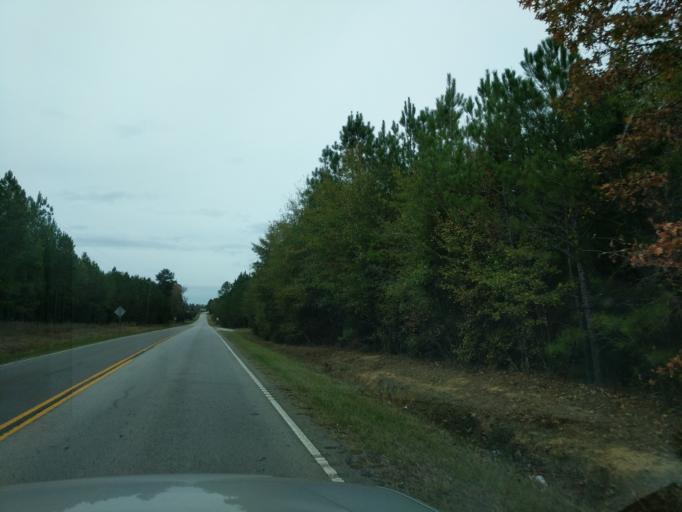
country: US
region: South Carolina
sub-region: Saluda County
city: Saluda
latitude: 34.0283
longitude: -81.7689
